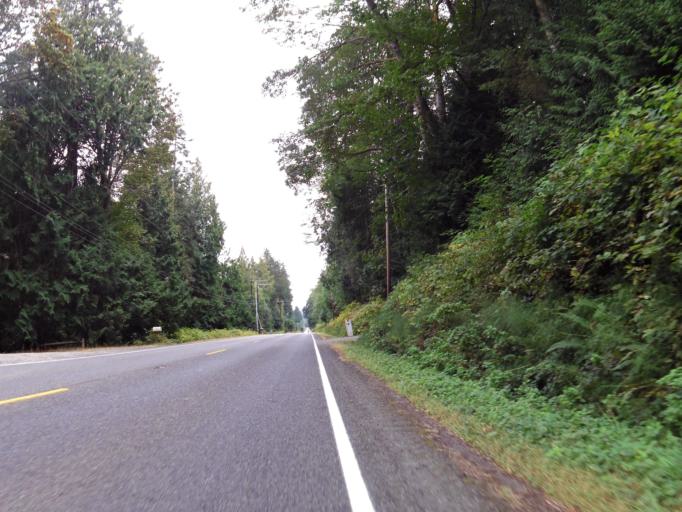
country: US
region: Washington
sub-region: Jefferson County
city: Port Hadlock-Irondale
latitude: 47.9983
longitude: -122.7237
